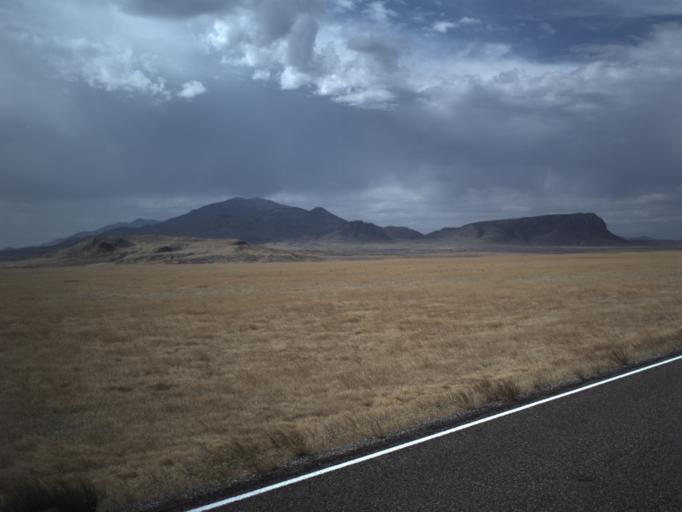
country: US
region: Utah
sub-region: Tooele County
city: Wendover
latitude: 41.3946
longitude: -113.9643
